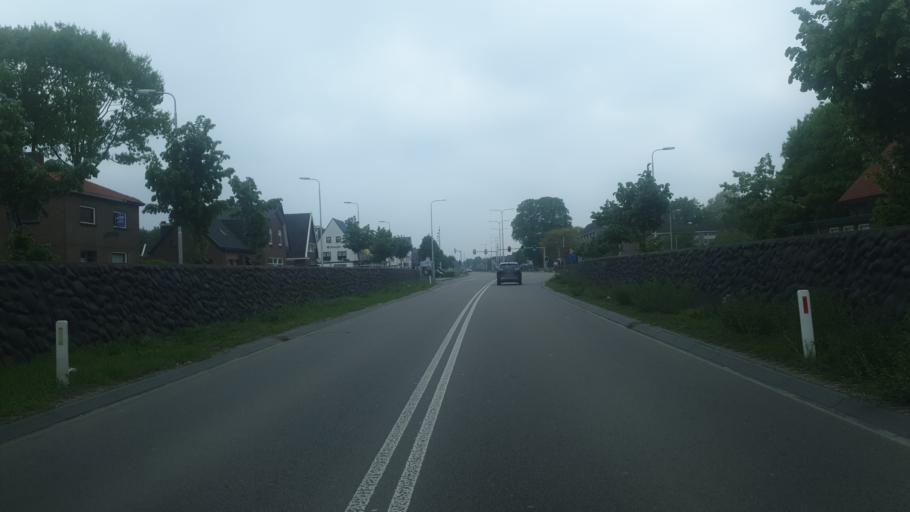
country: NL
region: Gelderland
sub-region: Gemeente Wijchen
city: Wijchen
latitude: 51.8050
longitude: 5.7569
